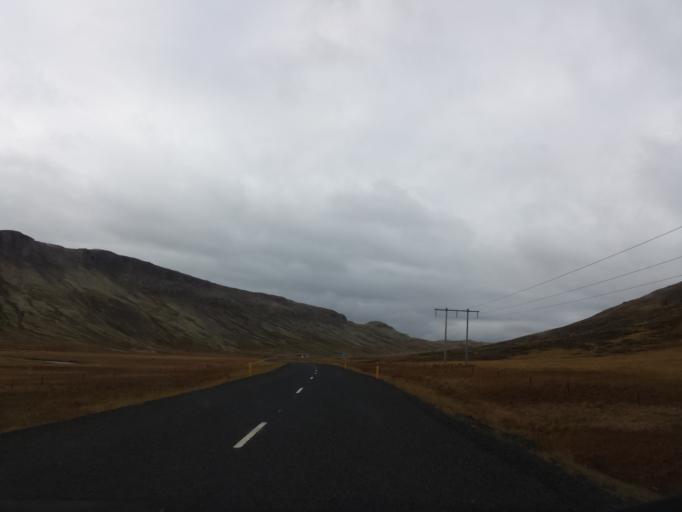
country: IS
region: West
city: Stykkisholmur
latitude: 64.8897
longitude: -22.8257
